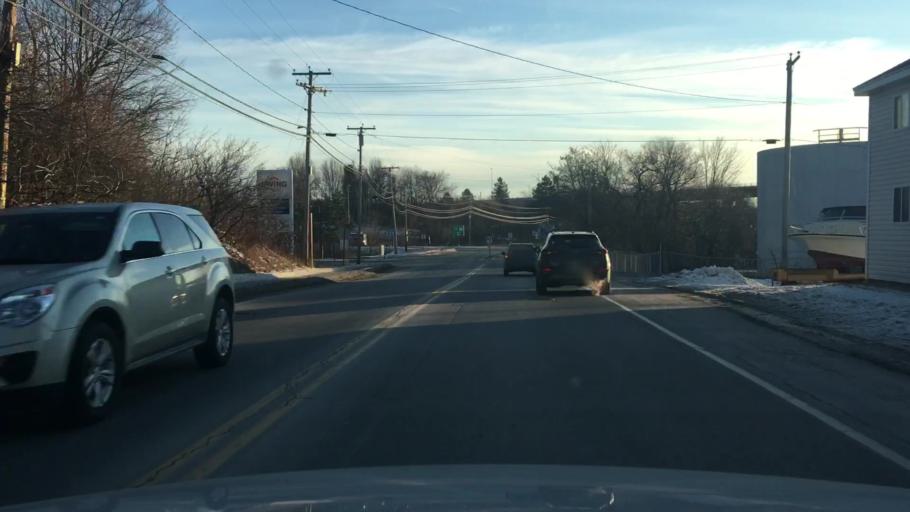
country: US
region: Maine
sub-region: Penobscot County
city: Brewer
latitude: 44.7870
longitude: -68.7708
